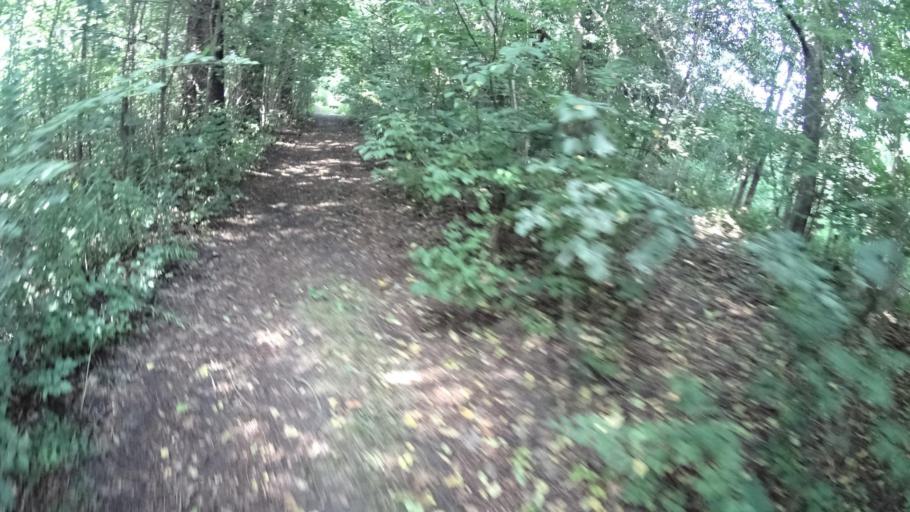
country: PL
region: Masovian Voivodeship
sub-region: Powiat piaseczynski
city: Lesznowola
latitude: 52.0248
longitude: 20.9045
